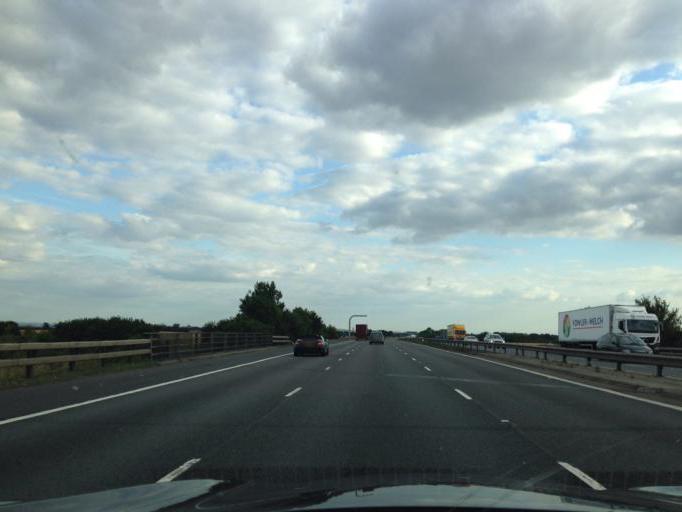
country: GB
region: England
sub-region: Oxfordshire
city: Bicester
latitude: 51.9293
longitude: -1.2018
